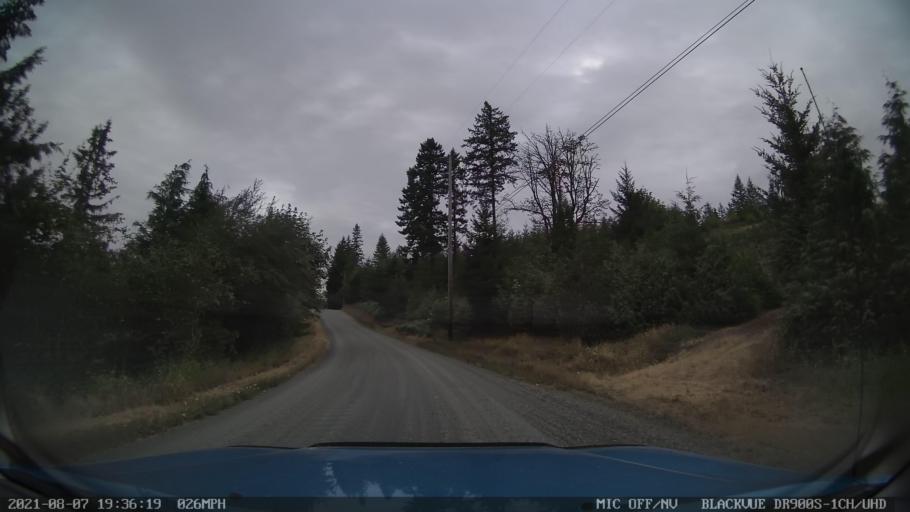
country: US
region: Oregon
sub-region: Marion County
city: Silverton
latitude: 44.9325
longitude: -122.6568
